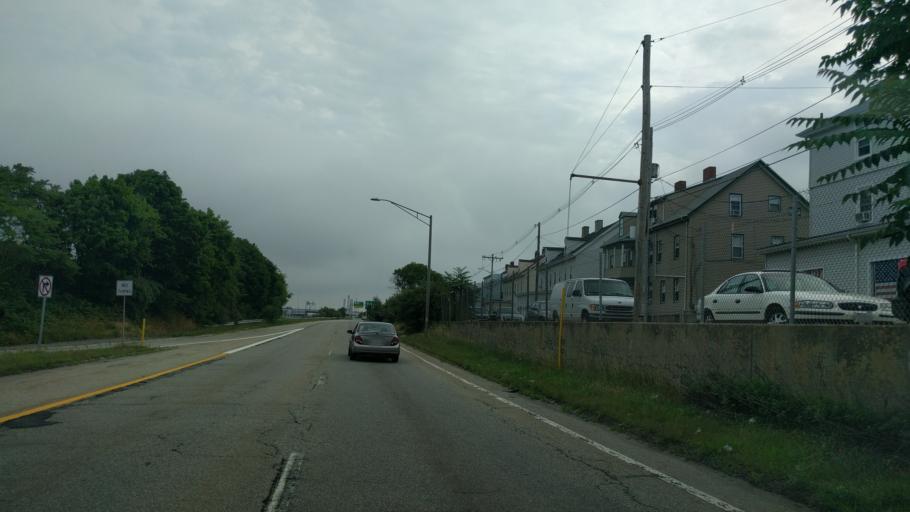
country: US
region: Massachusetts
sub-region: Bristol County
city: Fall River
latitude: 41.7193
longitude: -71.1532
